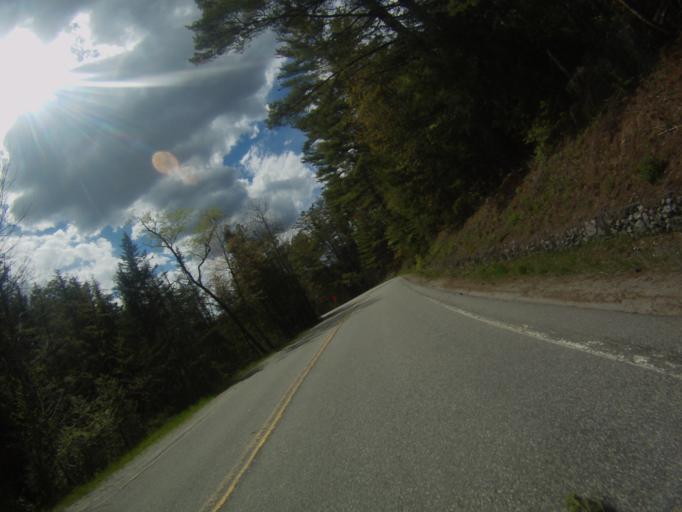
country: US
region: New York
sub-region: Essex County
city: Mineville
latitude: 44.0769
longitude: -73.6566
